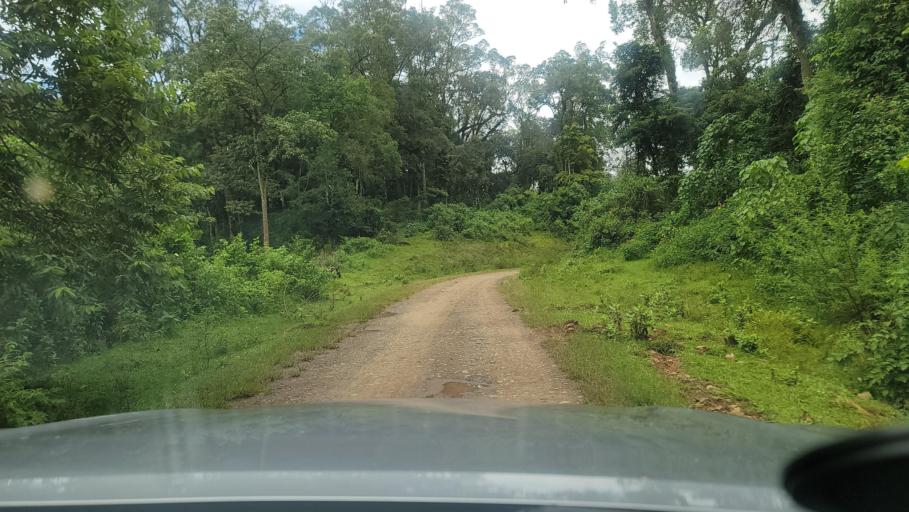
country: ET
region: Southern Nations, Nationalities, and People's Region
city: Bonga
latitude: 7.6254
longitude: 36.2117
